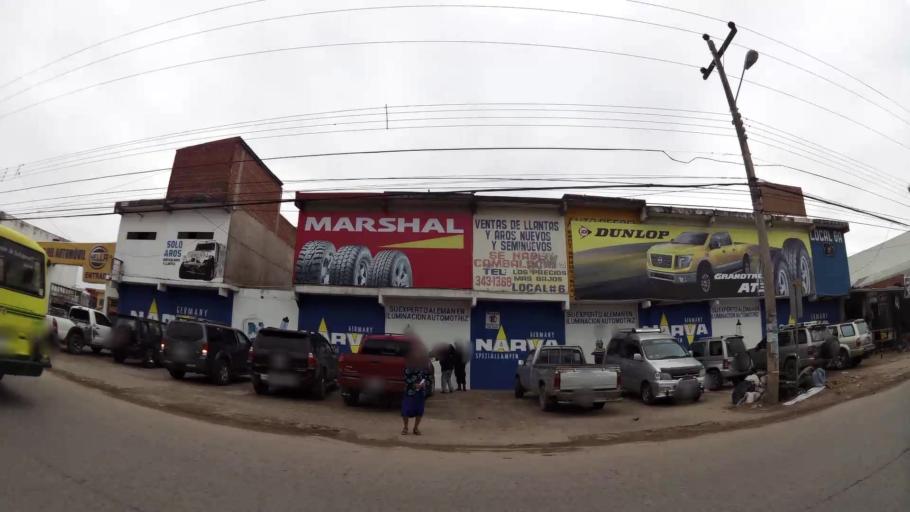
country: BO
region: Santa Cruz
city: Santa Cruz de la Sierra
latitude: -17.7506
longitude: -63.1883
